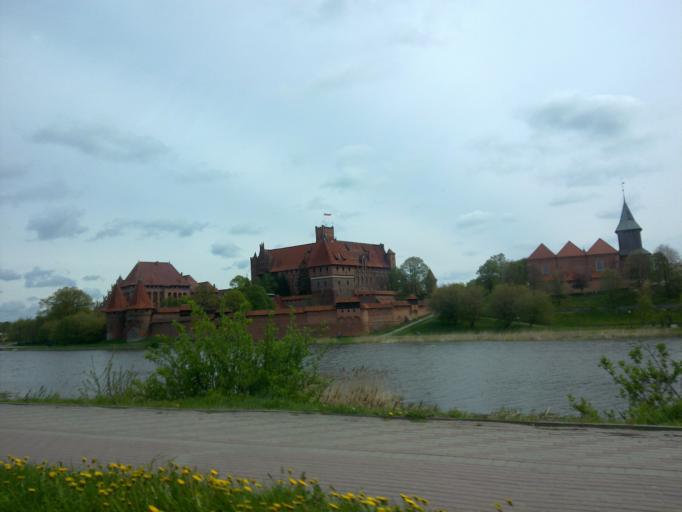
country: PL
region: Pomeranian Voivodeship
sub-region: Powiat malborski
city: Malbork
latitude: 54.0397
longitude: 19.0229
